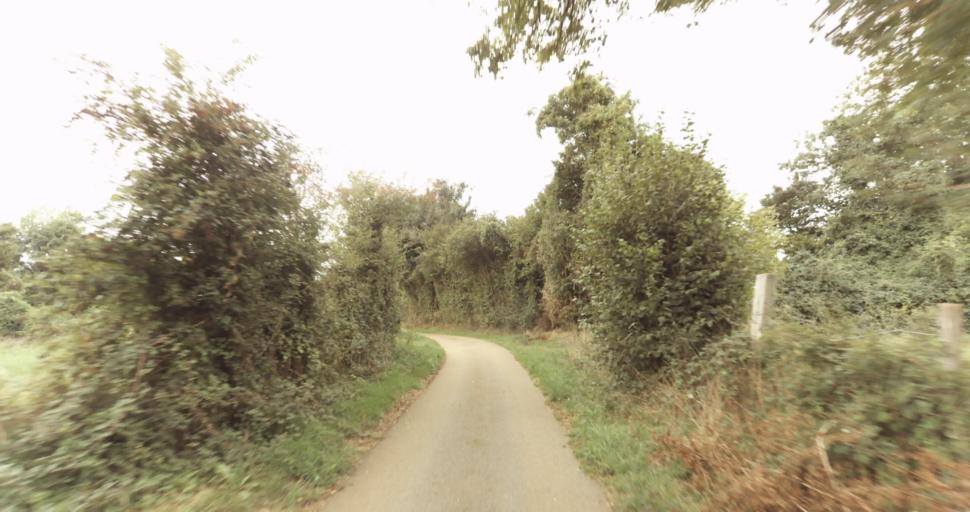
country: FR
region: Lower Normandy
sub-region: Departement de l'Orne
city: Gace
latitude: 48.7612
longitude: 0.3228
